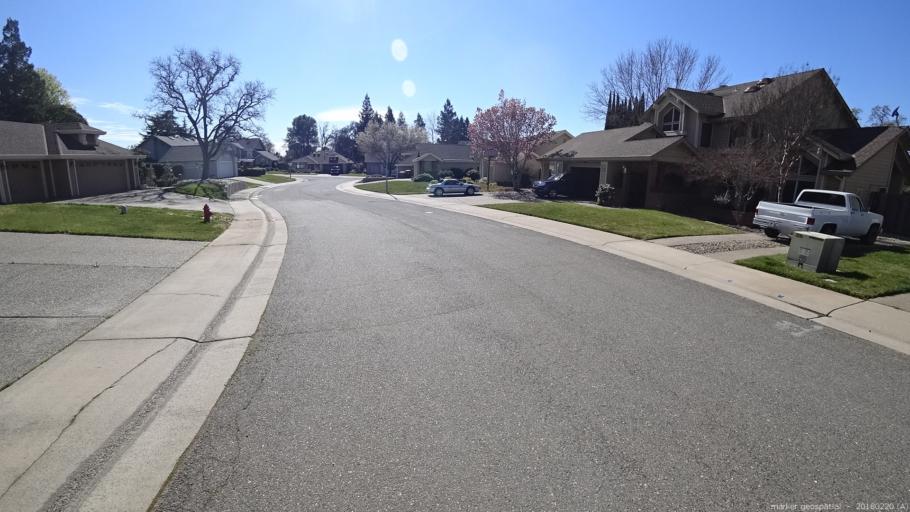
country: US
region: California
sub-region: Sacramento County
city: Orangevale
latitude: 38.6763
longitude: -121.2219
